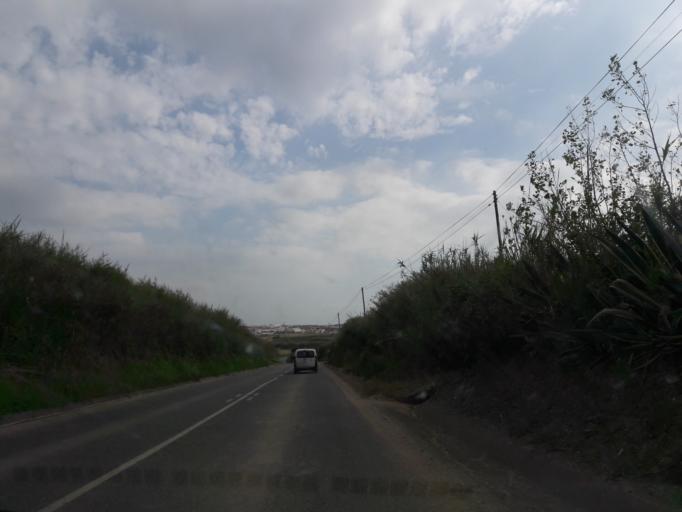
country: PT
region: Leiria
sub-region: Peniche
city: Atouguia da Baleia
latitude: 39.3503
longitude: -9.3232
